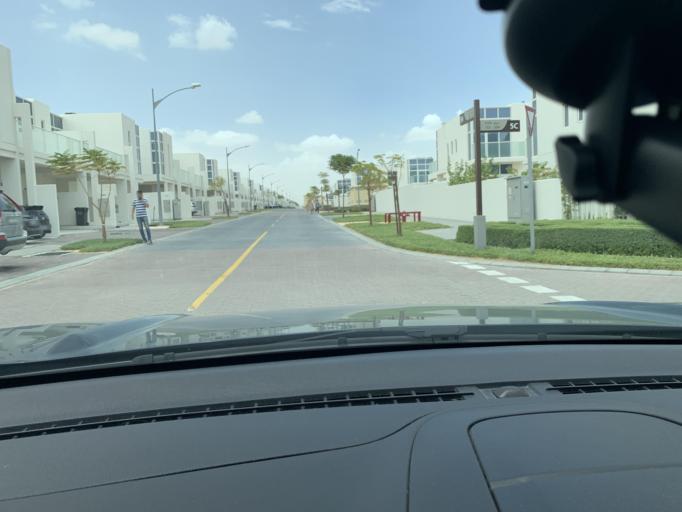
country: AE
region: Dubai
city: Dubai
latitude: 24.9943
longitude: 55.3710
